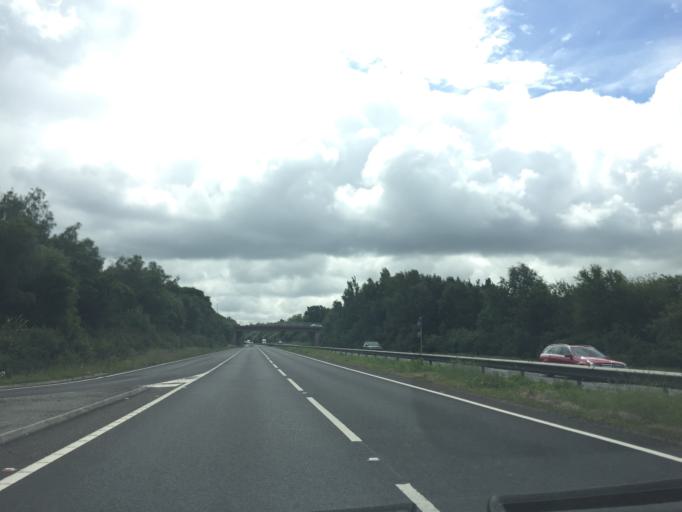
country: GB
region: England
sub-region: Dorset
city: Ferndown
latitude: 50.8170
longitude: -1.8902
